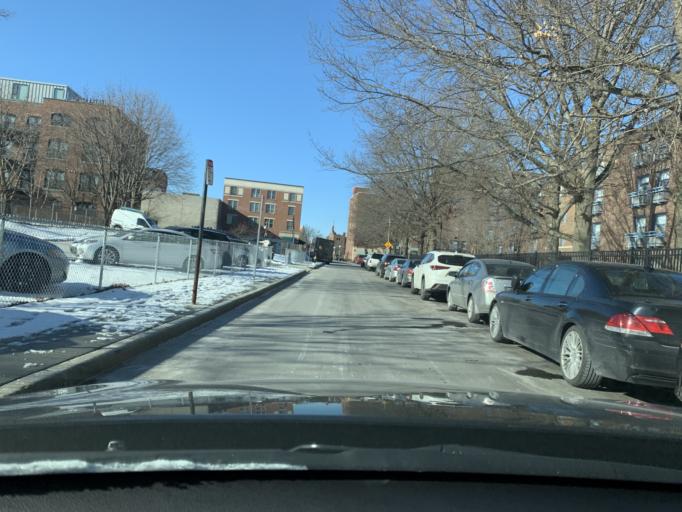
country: US
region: Massachusetts
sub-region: Suffolk County
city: South Boston
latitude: 42.3341
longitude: -71.0776
